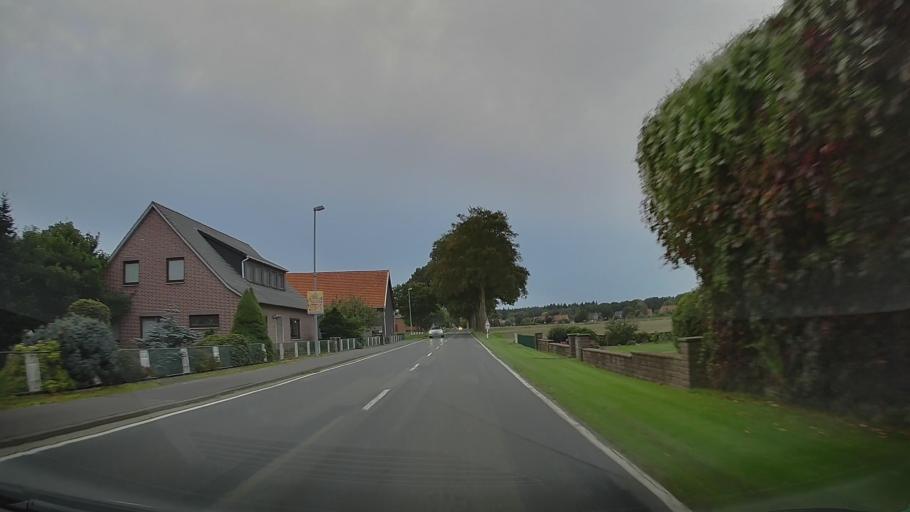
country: DE
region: Lower Saxony
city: Syke
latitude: 52.9059
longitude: 8.8749
